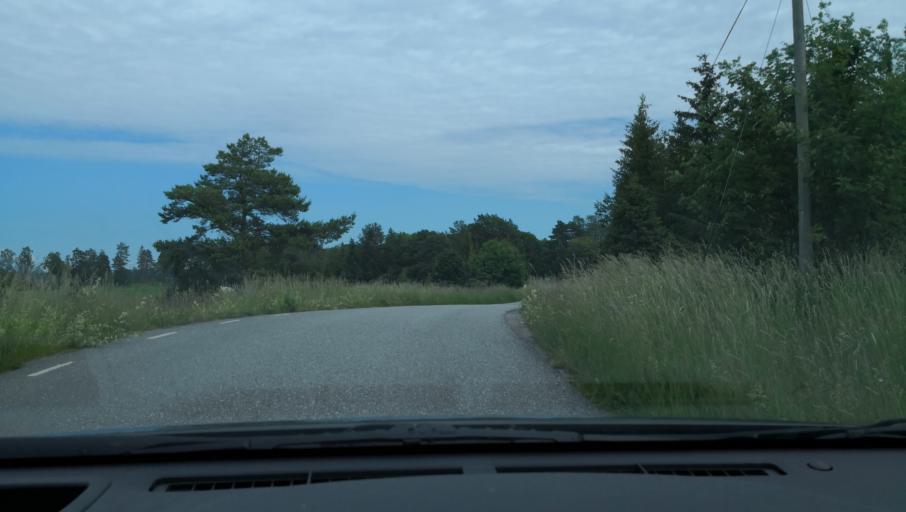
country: SE
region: Uppsala
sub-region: Enkopings Kommun
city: Orsundsbro
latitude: 59.6912
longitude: 17.3856
